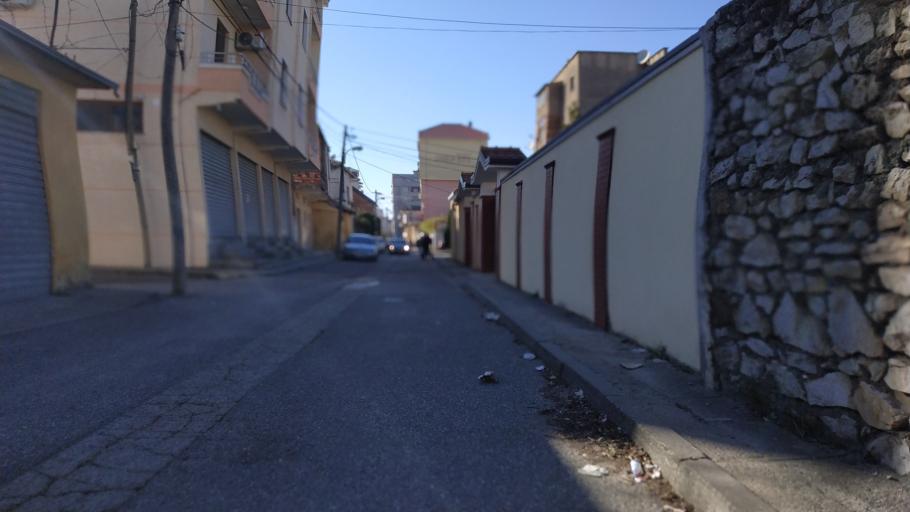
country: AL
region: Shkoder
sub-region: Rrethi i Shkodres
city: Shkoder
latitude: 42.0710
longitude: 19.5128
